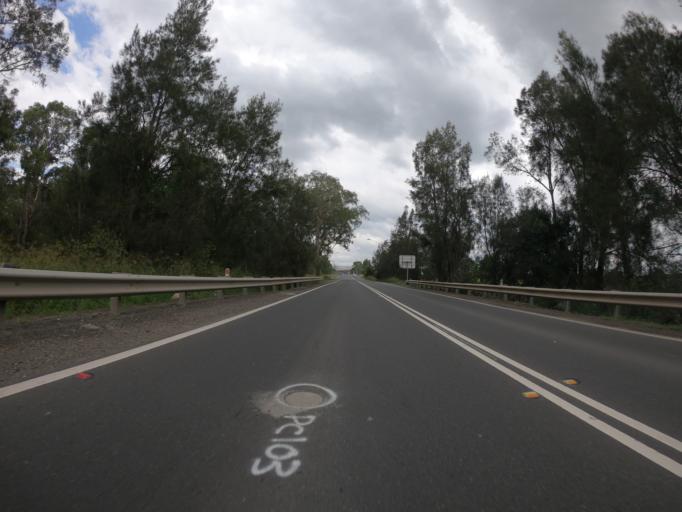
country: AU
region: New South Wales
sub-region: Blacktown
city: Mount Druitt
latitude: -33.8136
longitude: 150.7759
